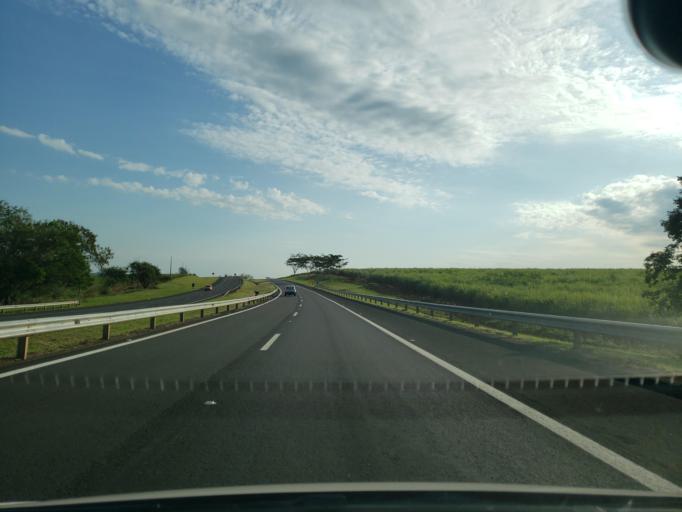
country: BR
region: Sao Paulo
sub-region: Valparaiso
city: Valparaiso
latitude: -21.2044
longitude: -50.8071
